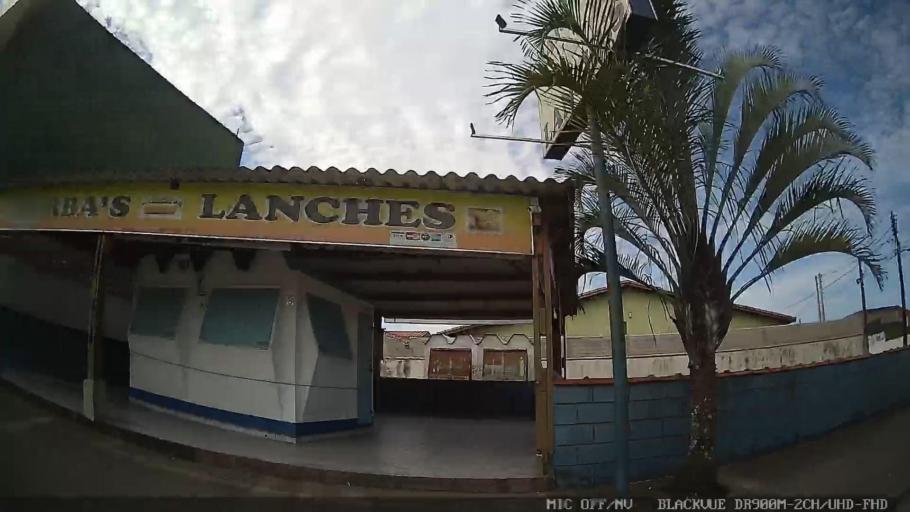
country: BR
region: Sao Paulo
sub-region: Itanhaem
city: Itanhaem
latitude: -24.1594
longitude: -46.7662
